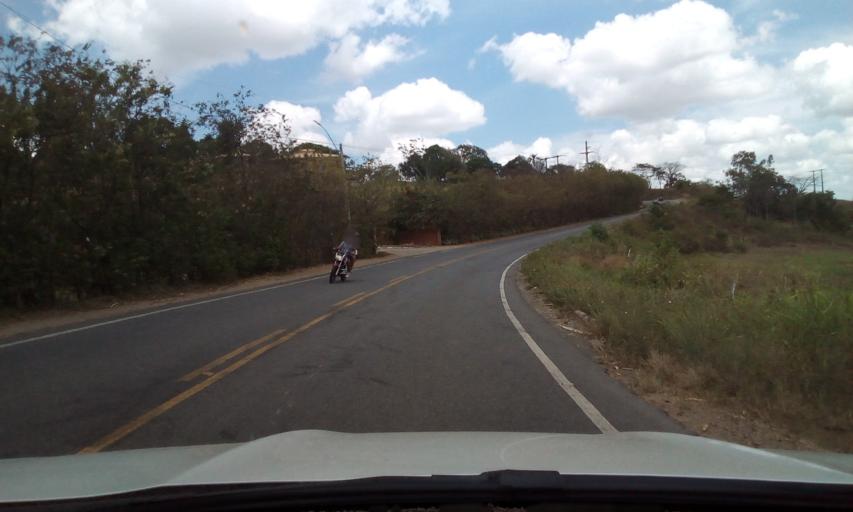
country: BR
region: Paraiba
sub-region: Guarabira
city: Guarabira
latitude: -6.8895
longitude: -35.5093
